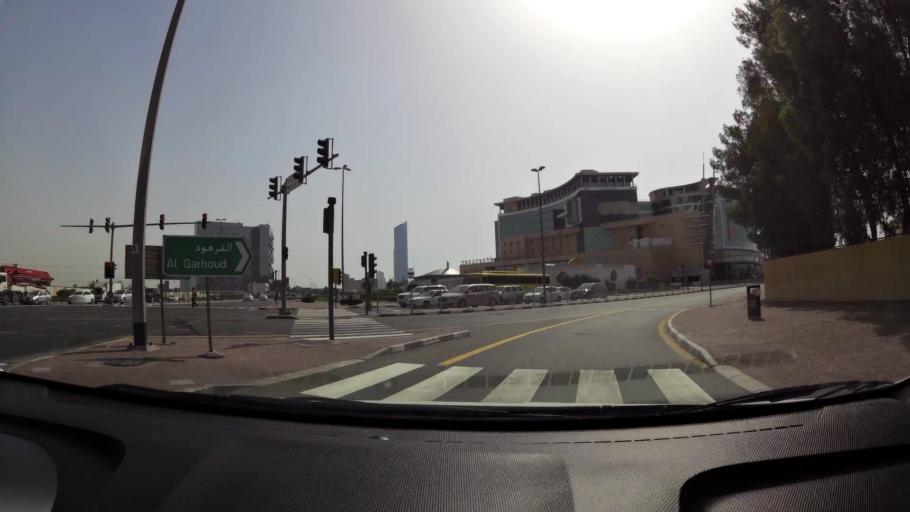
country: AE
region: Ash Shariqah
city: Sharjah
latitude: 25.2339
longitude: 55.3584
